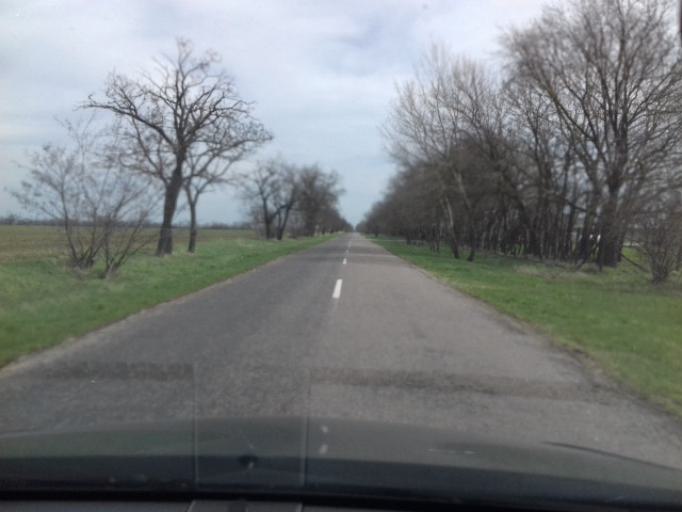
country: HU
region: Jasz-Nagykun-Szolnok
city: Cserkeszolo
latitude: 46.9014
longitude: 20.1708
